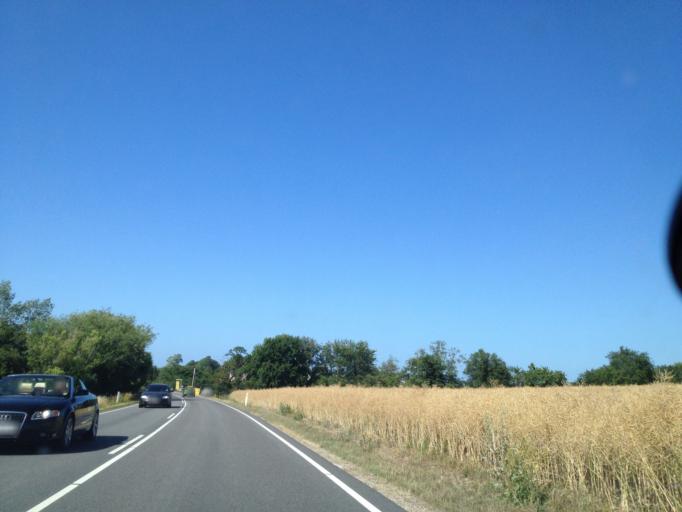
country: DK
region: Capital Region
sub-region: Gribskov Kommune
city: Graested
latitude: 56.0692
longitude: 12.3454
